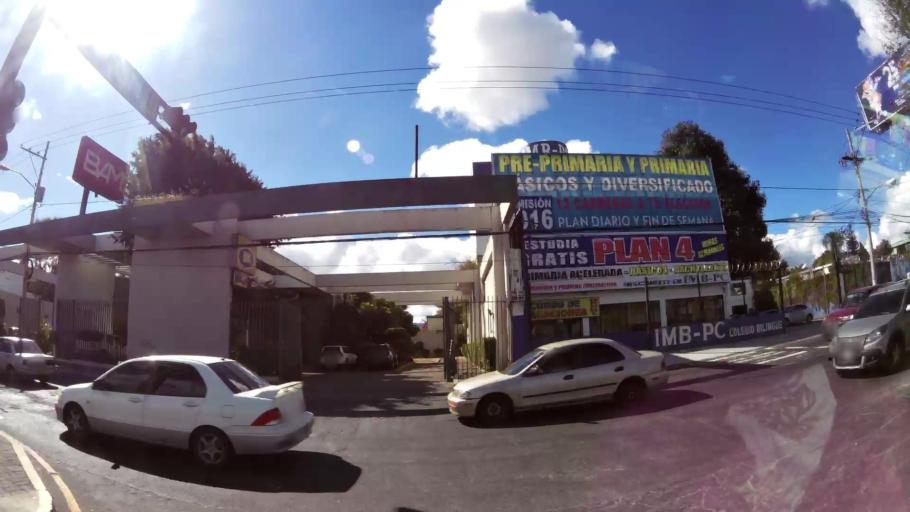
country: GT
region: Guatemala
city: Santa Catarina Pinula
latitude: 14.5899
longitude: -90.5450
